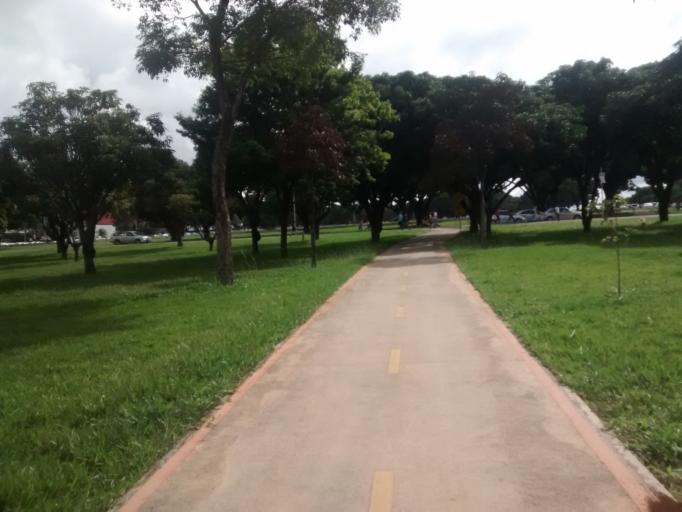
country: BR
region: Federal District
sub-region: Brasilia
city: Brasilia
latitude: -15.7856
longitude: -47.9068
